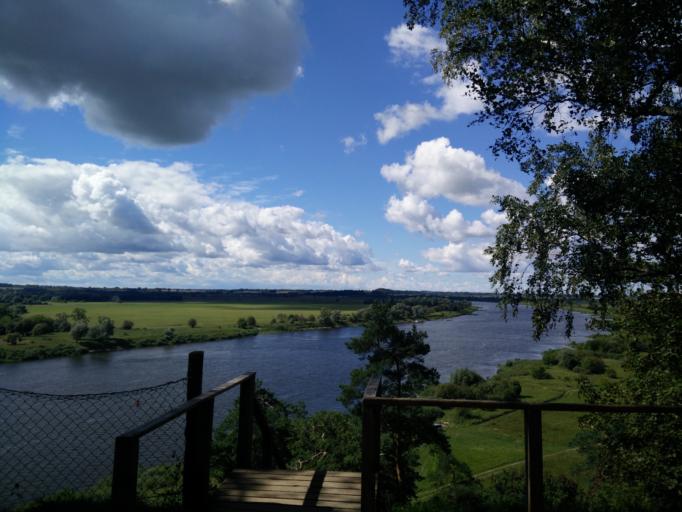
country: RU
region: Kaliningrad
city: Neman
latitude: 55.0877
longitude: 22.0208
